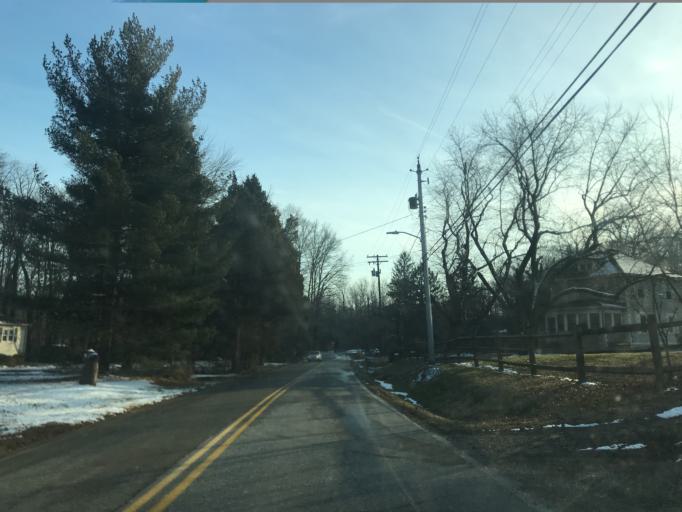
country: US
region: Maryland
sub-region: Harford County
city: Edgewood
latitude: 39.4049
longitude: -76.3247
